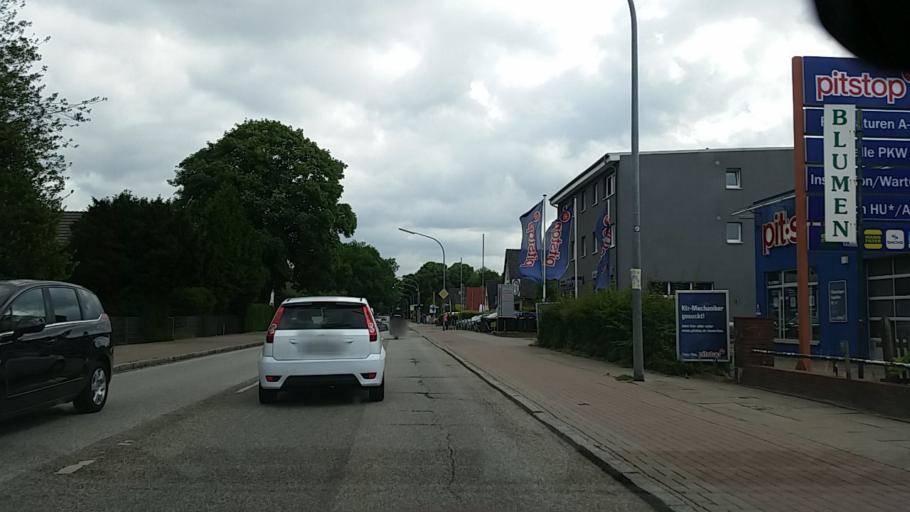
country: DE
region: Hamburg
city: Langenhorn
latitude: 53.6855
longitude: 10.0233
